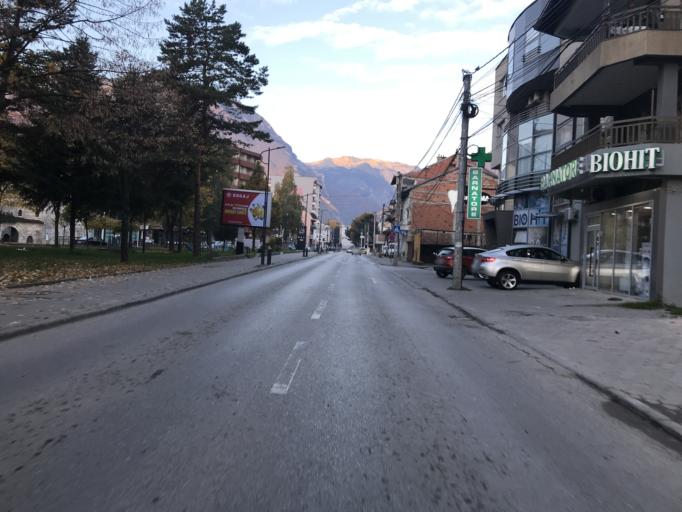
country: XK
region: Pec
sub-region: Komuna e Pejes
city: Peje
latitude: 42.6619
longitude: 20.2882
